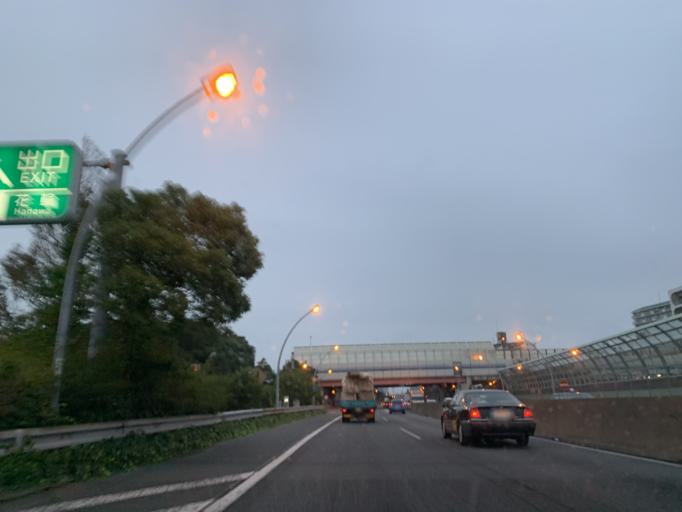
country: JP
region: Chiba
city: Funabashi
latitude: 35.6852
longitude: 140.0029
